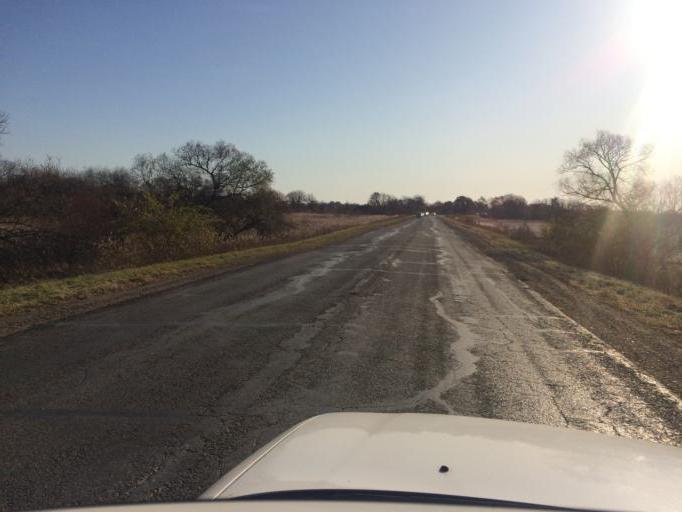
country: RU
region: Primorskiy
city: Dal'nerechensk
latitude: 45.9176
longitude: 133.7781
